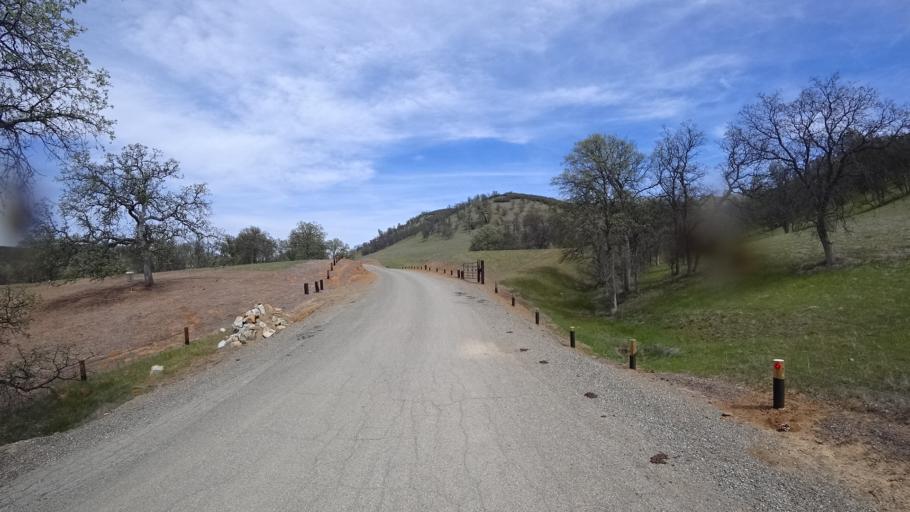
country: US
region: California
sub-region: Glenn County
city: Willows
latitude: 39.5890
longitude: -122.5234
